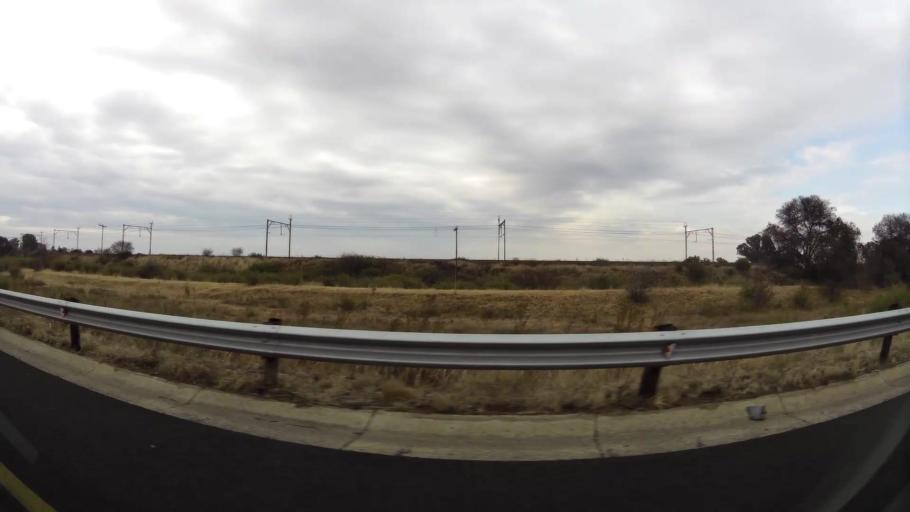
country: ZA
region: Orange Free State
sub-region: Fezile Dabi District Municipality
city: Kroonstad
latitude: -27.6336
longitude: 27.2499
